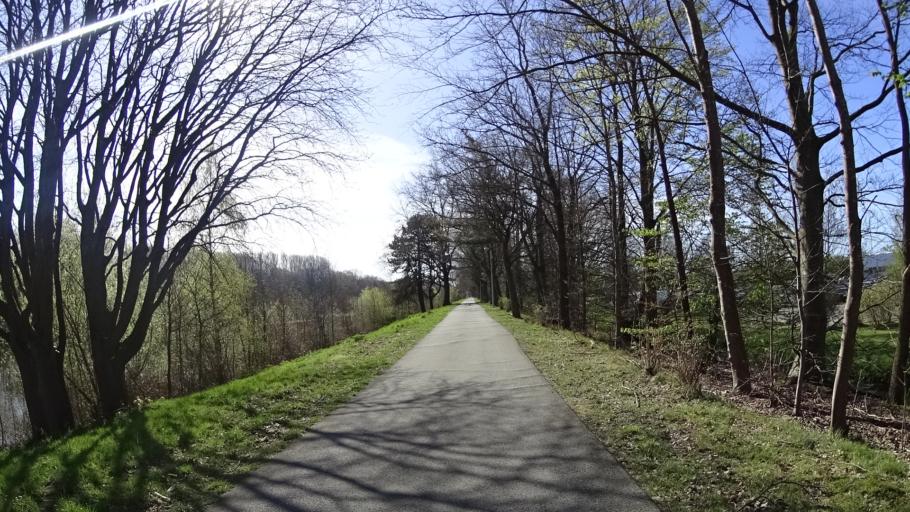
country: DE
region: Lower Saxony
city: Meppen
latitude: 52.6837
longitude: 7.3006
